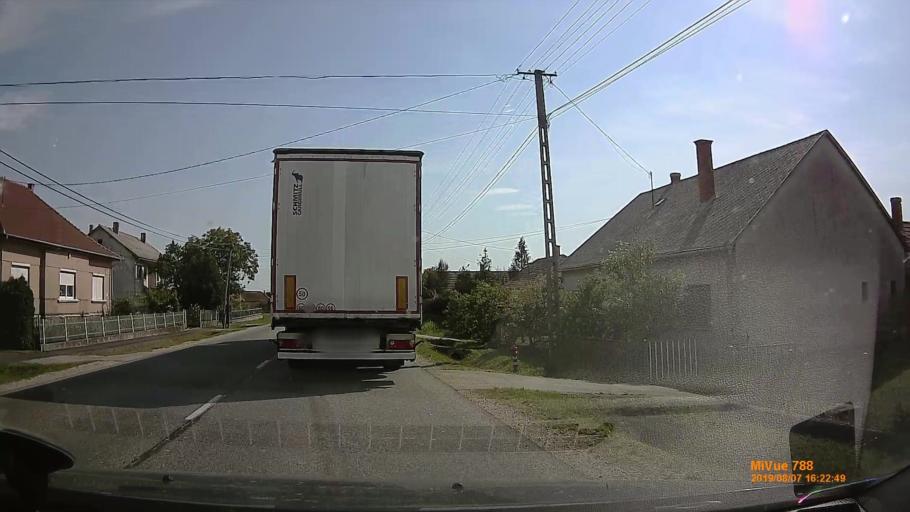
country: HU
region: Zala
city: Zalalovo
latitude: 46.7530
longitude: 16.5592
